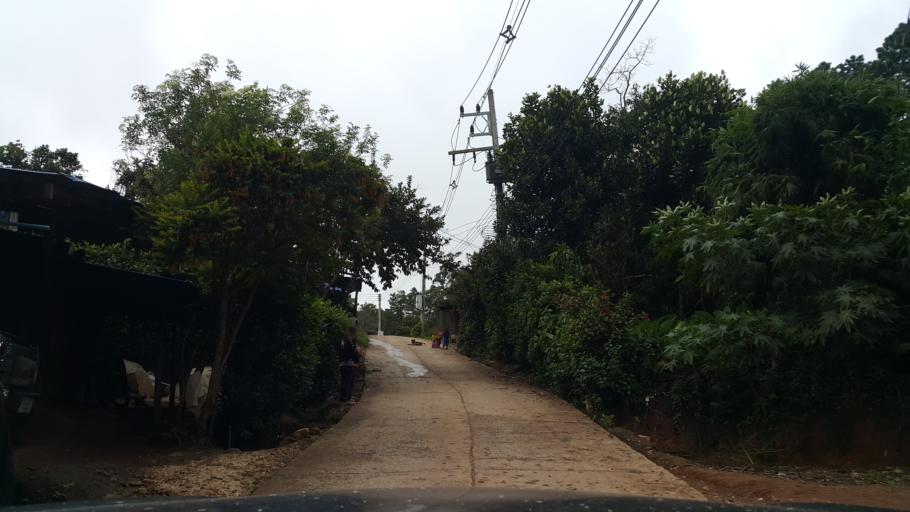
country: TH
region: Chiang Mai
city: Samoeng
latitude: 18.8807
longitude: 98.5134
